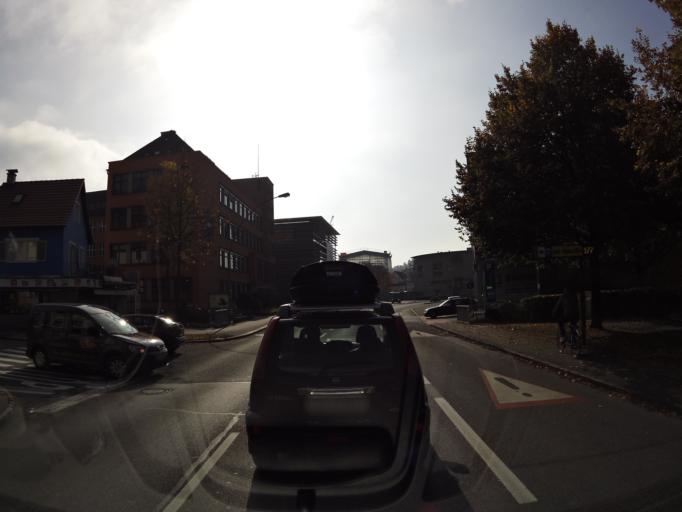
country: AT
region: Vorarlberg
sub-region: Politischer Bezirk Bregenz
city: Bregenz
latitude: 47.5069
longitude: 9.7505
